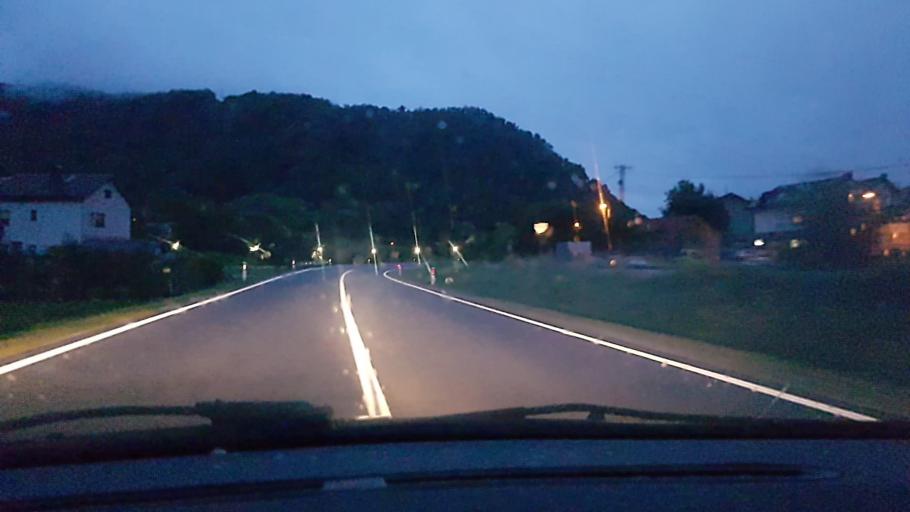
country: HR
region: Krapinsko-Zagorska
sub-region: Grad Krapina
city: Krapina
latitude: 46.1763
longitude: 15.8633
